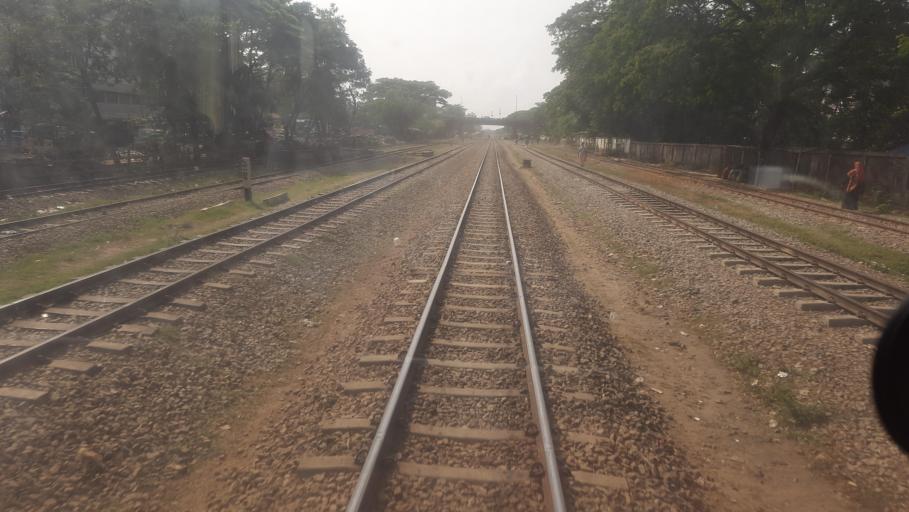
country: BD
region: Chittagong
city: Chittagong
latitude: 22.3392
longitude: 91.8166
